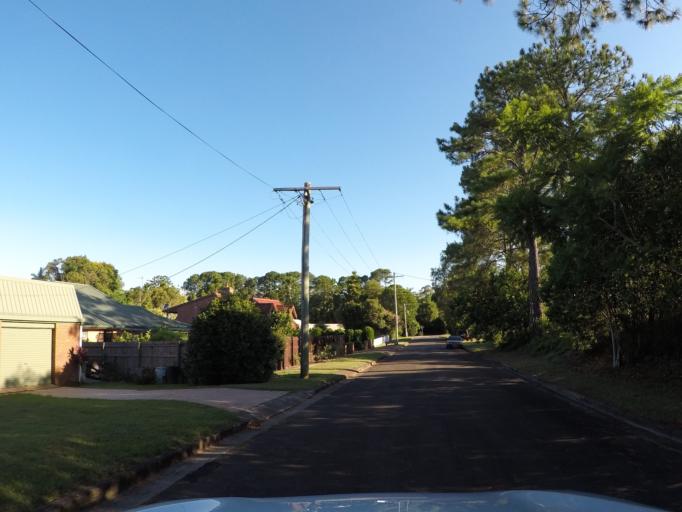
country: AU
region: Queensland
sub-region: Sunshine Coast
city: Nambour
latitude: -26.6290
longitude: 152.8680
